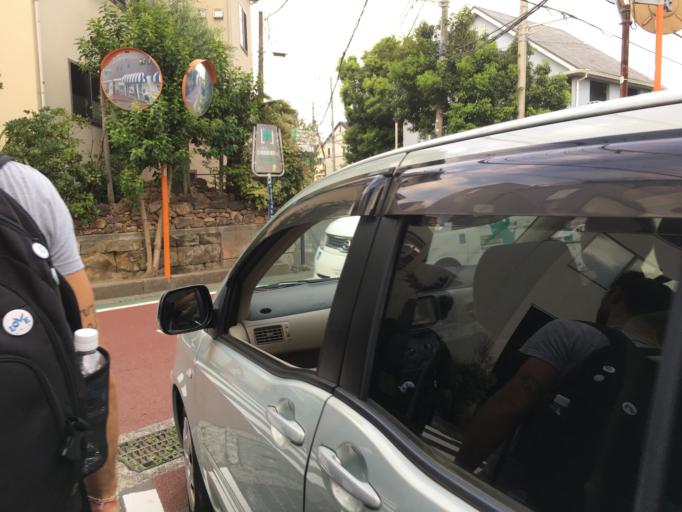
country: JP
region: Kanagawa
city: Kamakura
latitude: 35.3125
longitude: 139.5416
